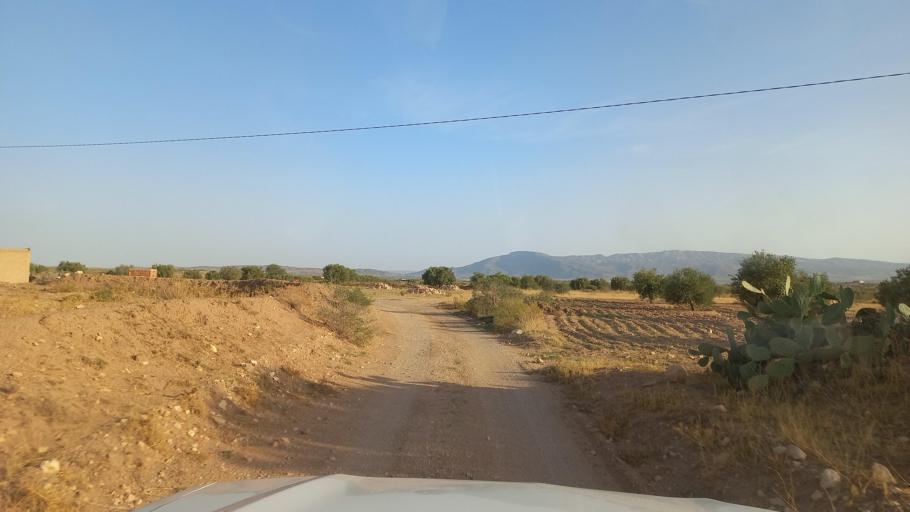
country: TN
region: Al Qasrayn
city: Kasserine
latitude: 35.2565
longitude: 8.9101
